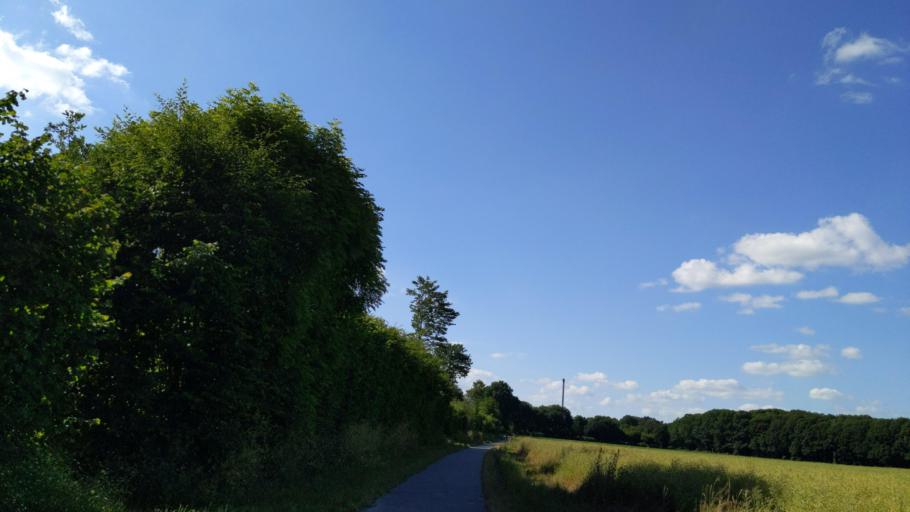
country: DE
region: Schleswig-Holstein
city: Klempau
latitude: 53.7692
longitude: 10.6627
